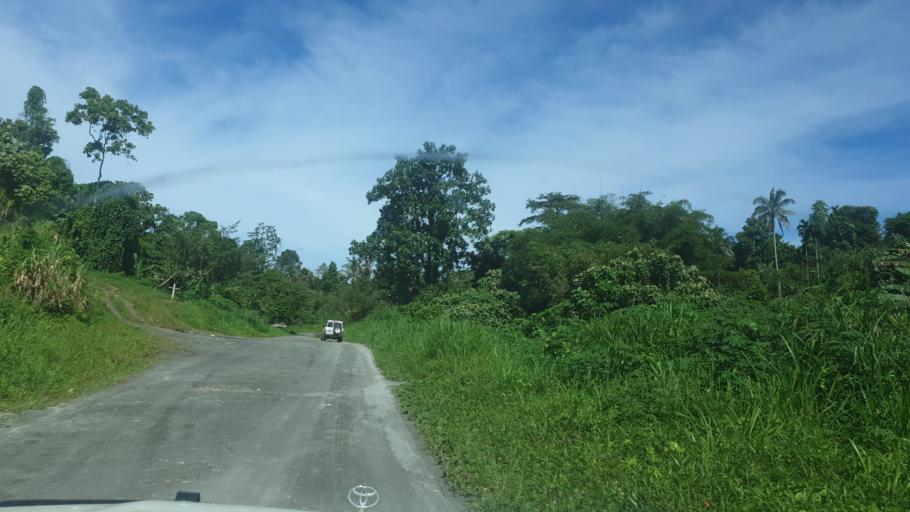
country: PG
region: Bougainville
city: Panguna
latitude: -6.5006
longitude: 155.3307
